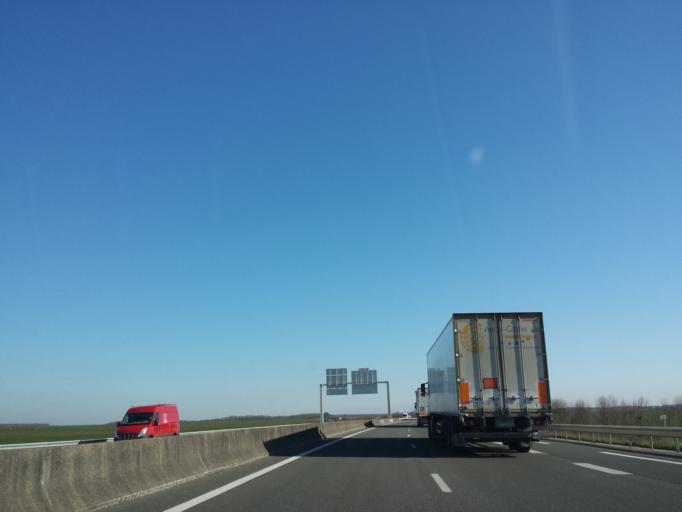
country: FR
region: Picardie
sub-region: Departement de l'Oise
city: Allonne
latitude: 49.4342
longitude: 2.1367
